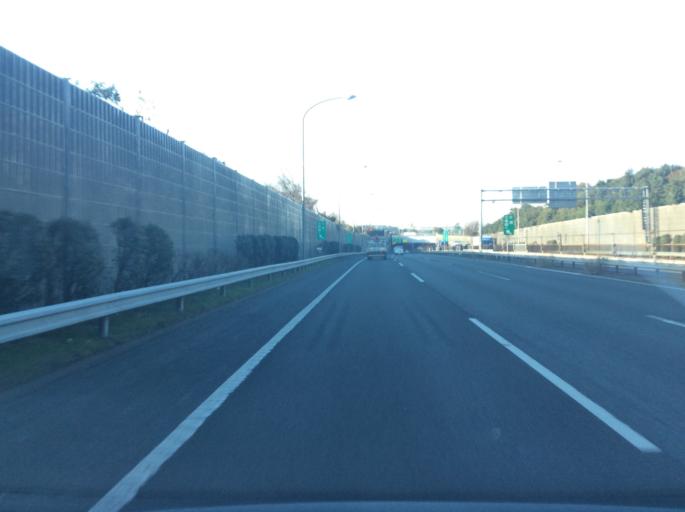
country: JP
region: Chiba
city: Nagareyama
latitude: 35.8560
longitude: 139.8786
